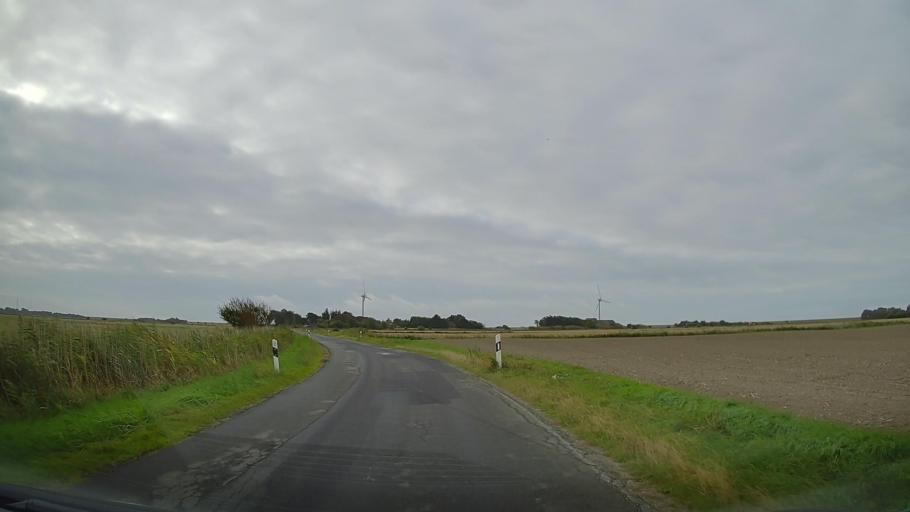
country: DE
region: Schleswig-Holstein
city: Emmelsbull-Horsbull
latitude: 54.8100
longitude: 8.6776
